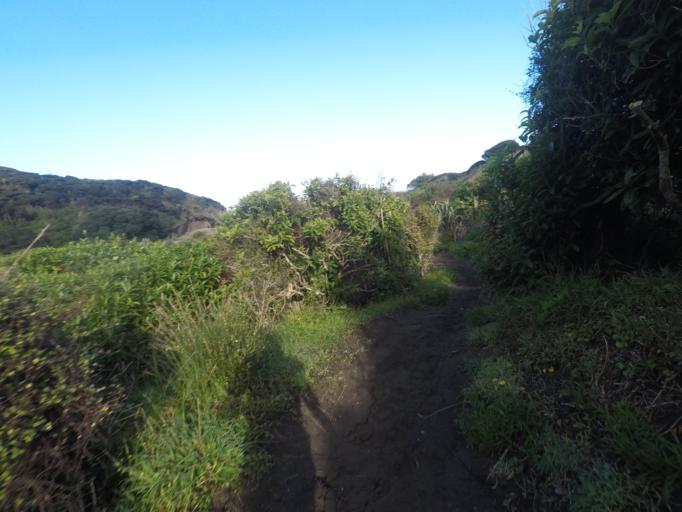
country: NZ
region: Auckland
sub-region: Auckland
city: Muriwai Beach
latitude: -36.9894
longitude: 174.4772
